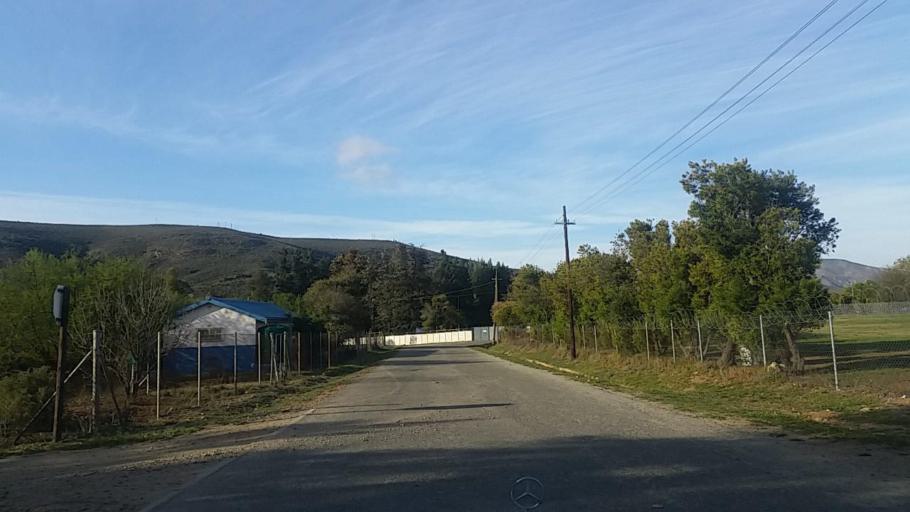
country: ZA
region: Western Cape
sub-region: Eden District Municipality
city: Knysna
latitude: -33.6569
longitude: 23.1219
